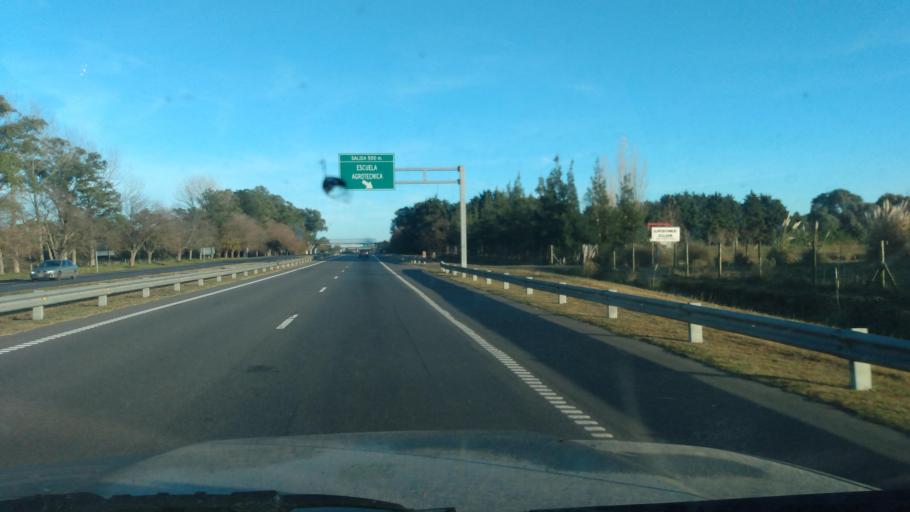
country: AR
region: Buenos Aires
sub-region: Partido de Lujan
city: Lujan
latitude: -34.5409
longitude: -59.2465
